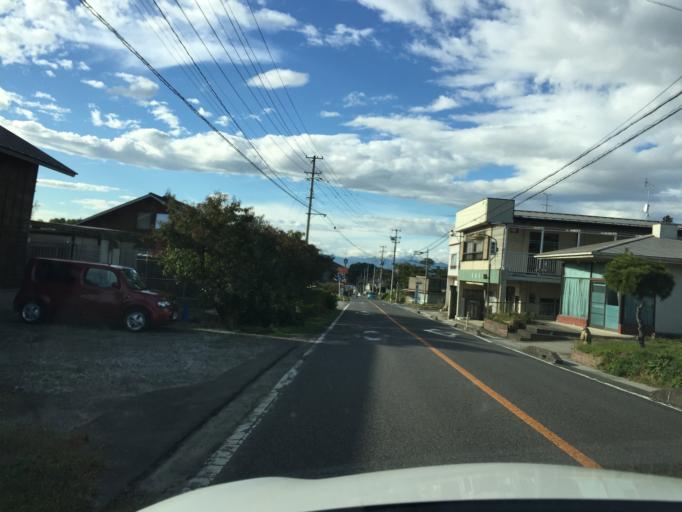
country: JP
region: Fukushima
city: Sukagawa
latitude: 37.2631
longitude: 140.4217
